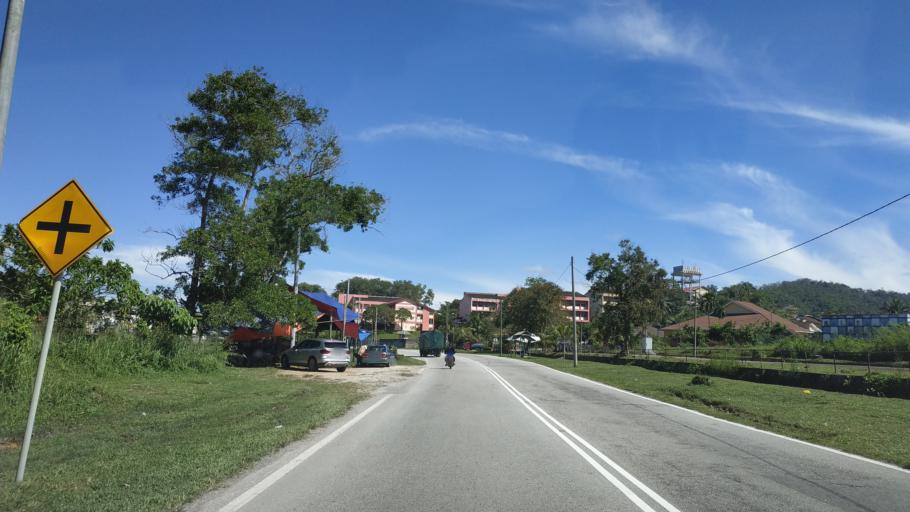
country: MY
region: Kedah
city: Kulim
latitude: 5.3366
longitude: 100.5376
